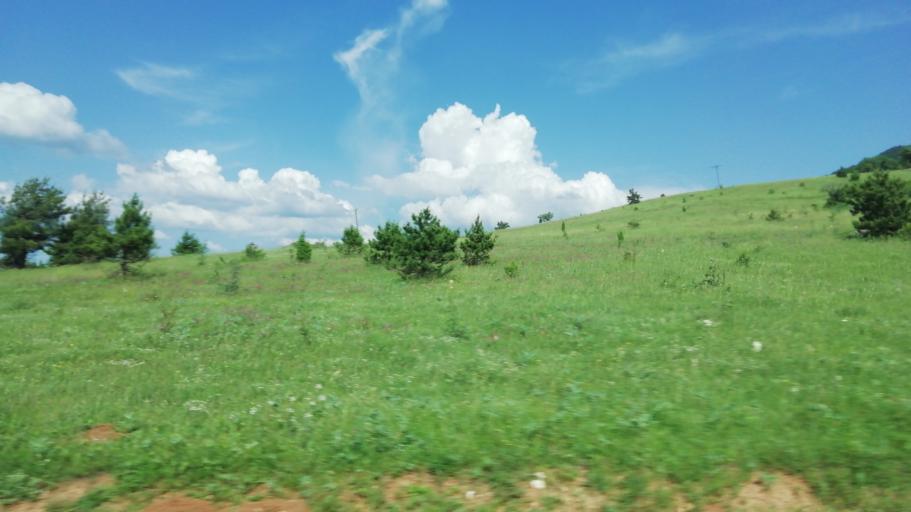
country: TR
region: Karabuk
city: Karabuk
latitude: 41.1279
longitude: 32.5756
